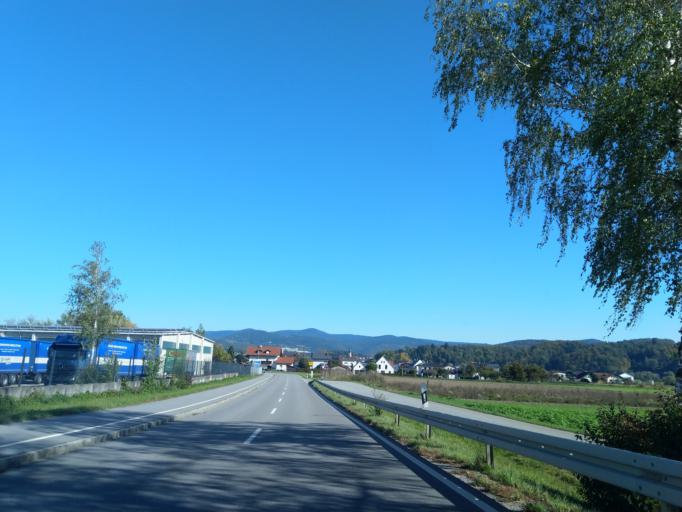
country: DE
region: Bavaria
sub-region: Lower Bavaria
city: Deggendorf
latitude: 48.8169
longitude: 12.9519
